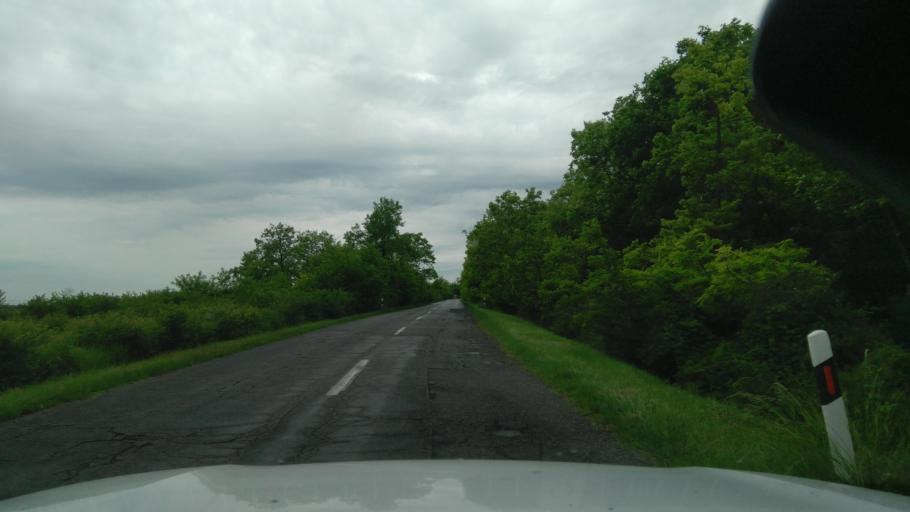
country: HU
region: Bekes
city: Bekescsaba
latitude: 46.6786
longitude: 21.1685
